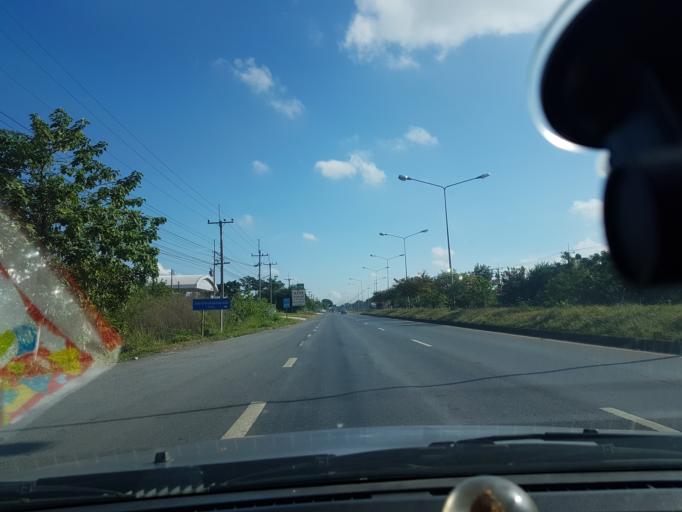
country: TH
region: Lop Buri
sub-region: Amphoe Tha Luang
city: Tha Luang
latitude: 15.0732
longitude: 100.9896
